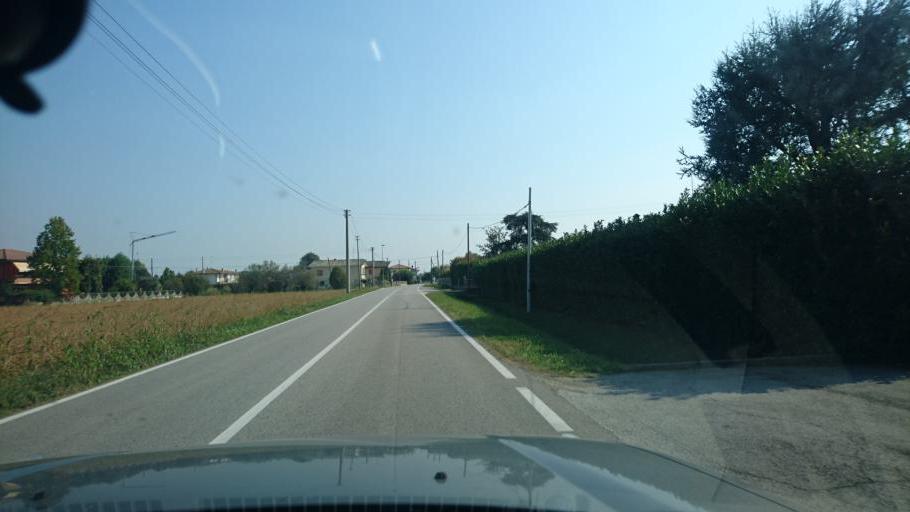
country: IT
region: Veneto
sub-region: Provincia di Padova
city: Ronchi di Campanile
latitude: 45.4721
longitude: 11.7868
